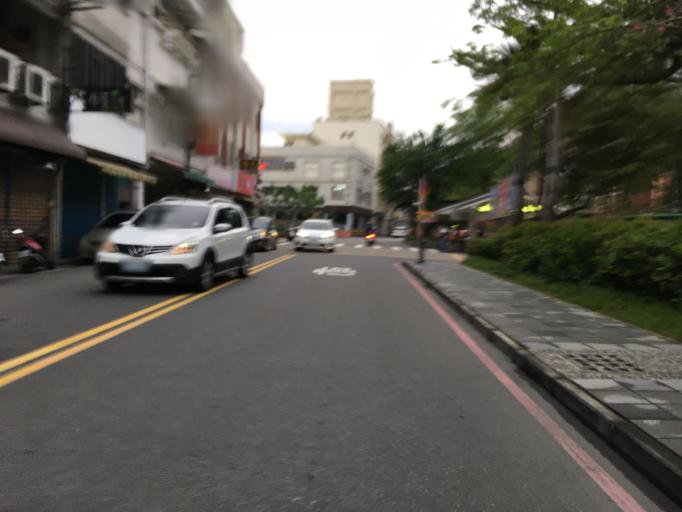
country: TW
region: Taiwan
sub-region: Yilan
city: Yilan
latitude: 24.6775
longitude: 121.7616
